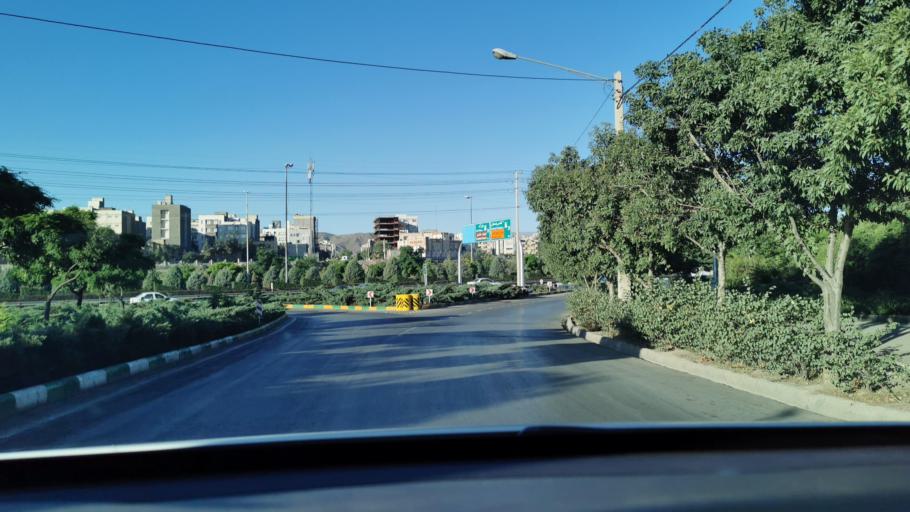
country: IR
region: Razavi Khorasan
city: Mashhad
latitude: 36.3476
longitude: 59.4770
